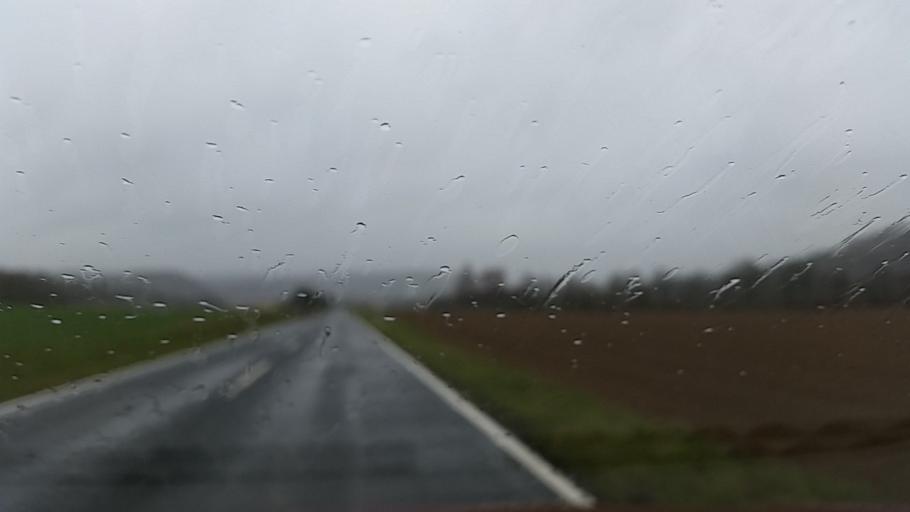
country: DE
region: Bavaria
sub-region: Regierungsbezirk Unterfranken
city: Himmelstadt
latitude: 49.9374
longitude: 9.7890
